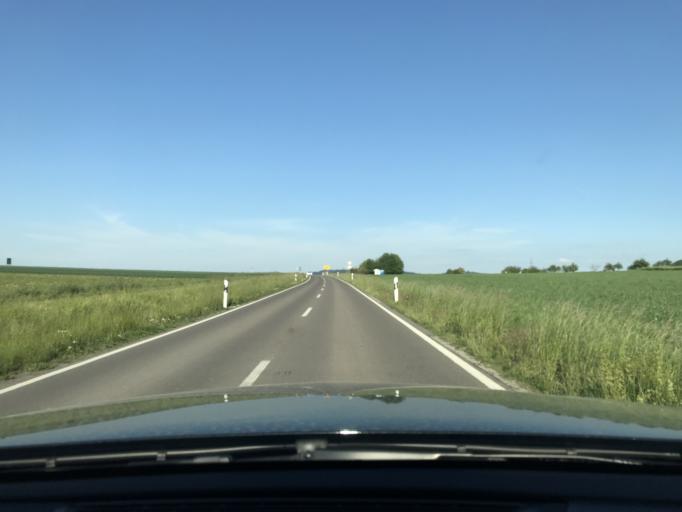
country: DE
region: Baden-Wuerttemberg
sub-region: Regierungsbezirk Stuttgart
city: Schwaikheim
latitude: 48.8928
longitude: 9.3600
